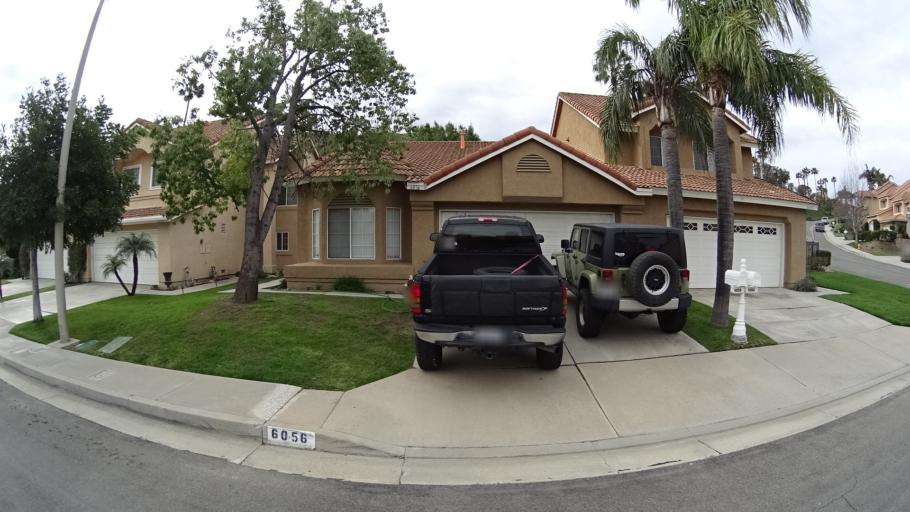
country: US
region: California
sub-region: Orange County
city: Villa Park
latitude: 33.8369
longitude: -117.7796
